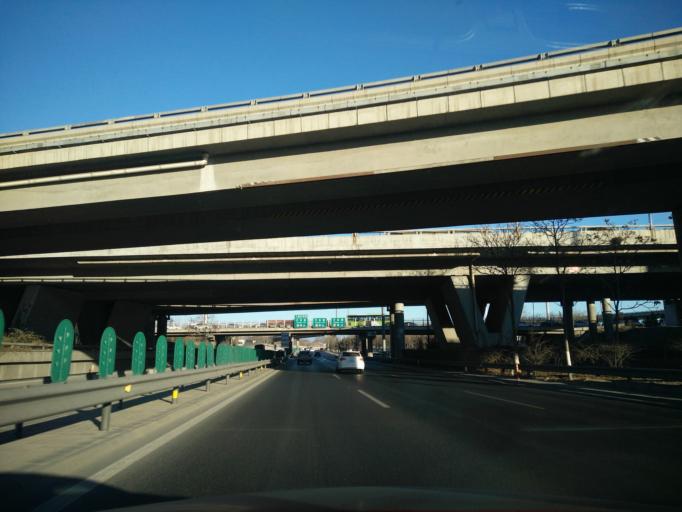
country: CN
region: Beijing
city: Lugu
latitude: 39.8439
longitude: 116.2193
